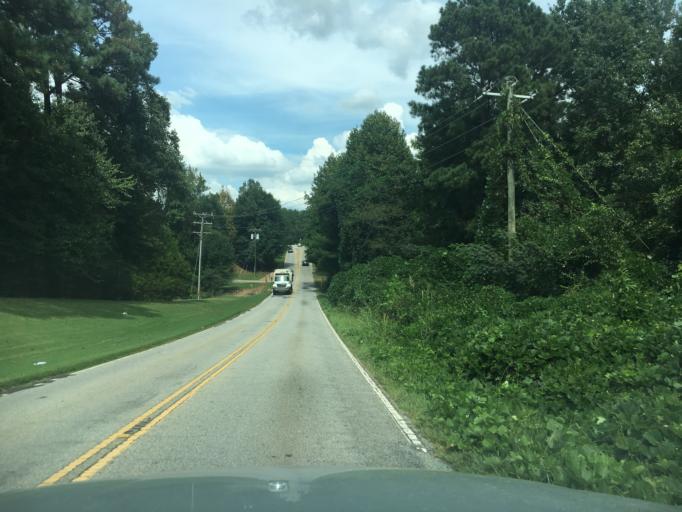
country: US
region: South Carolina
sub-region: Greenville County
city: Five Forks
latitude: 34.8139
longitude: -82.2313
